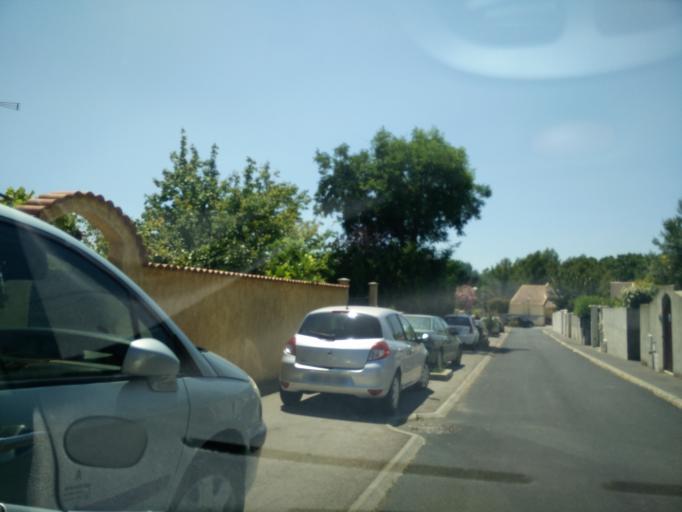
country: FR
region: Languedoc-Roussillon
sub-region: Departement de l'Herault
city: Saint-Christol
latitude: 43.7142
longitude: 4.0994
